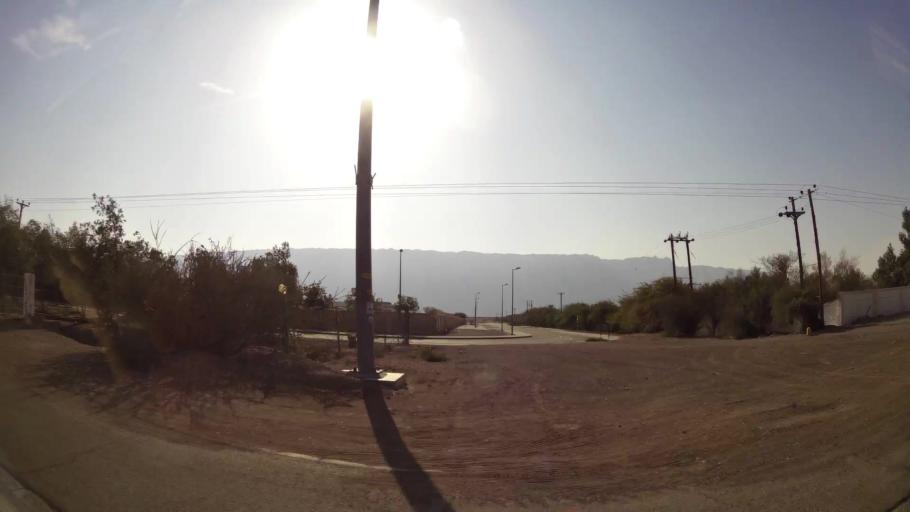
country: AE
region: Abu Dhabi
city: Al Ain
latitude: 24.0468
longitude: 55.8418
